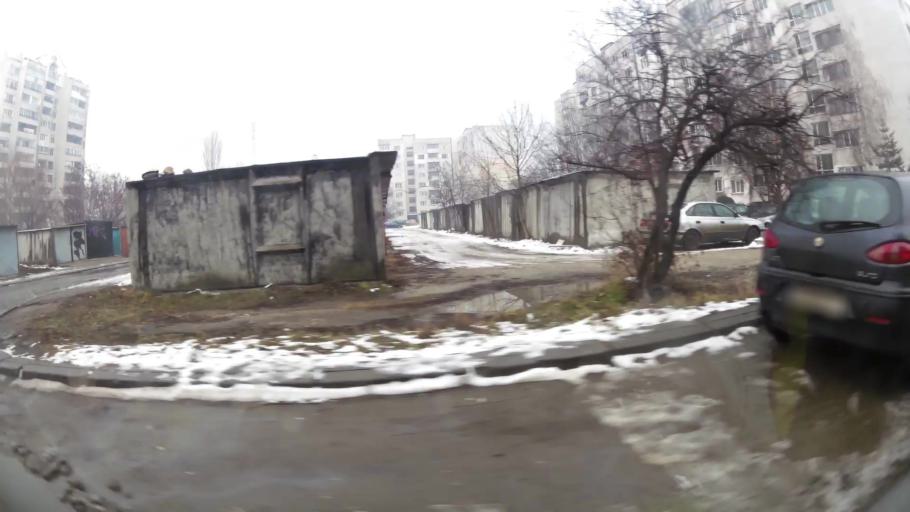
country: BG
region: Sofia-Capital
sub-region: Stolichna Obshtina
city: Sofia
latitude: 42.6881
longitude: 23.2603
